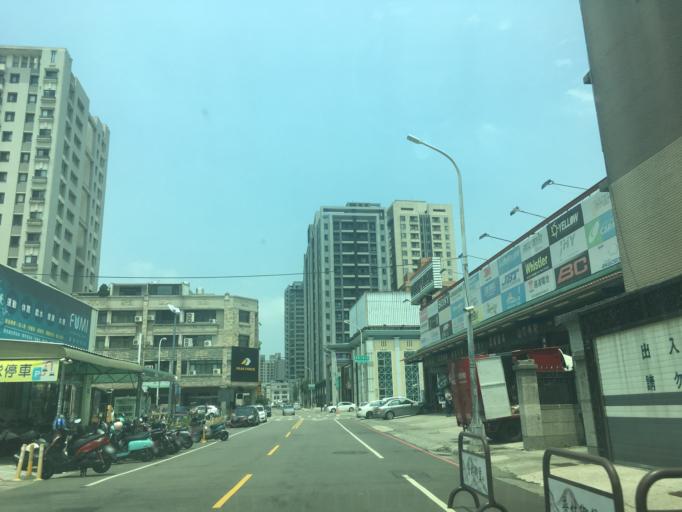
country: TW
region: Taiwan
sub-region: Taichung City
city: Taichung
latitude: 24.1773
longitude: 120.6823
